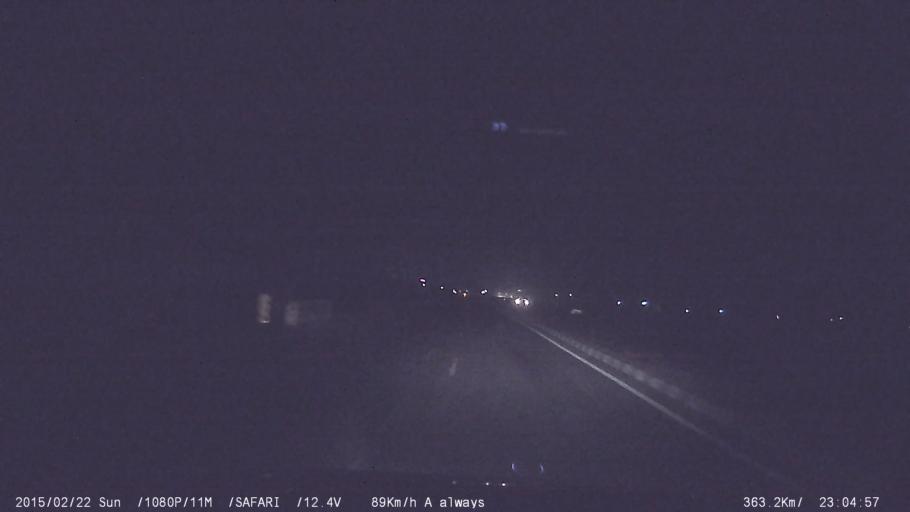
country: IN
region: Tamil Nadu
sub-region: Namakkal
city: Rasipuram
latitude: 11.4088
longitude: 78.1591
